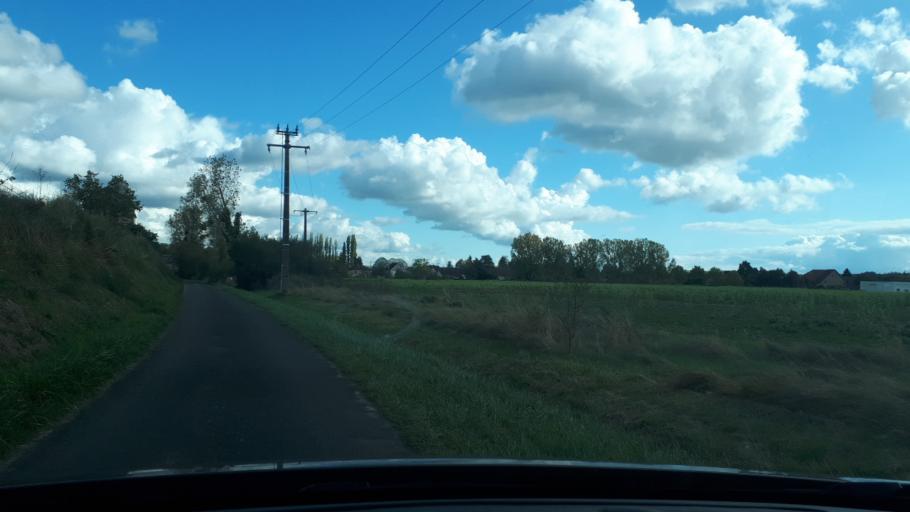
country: FR
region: Centre
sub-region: Departement du Loir-et-Cher
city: Saint-Aignan
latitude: 47.2878
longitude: 1.3801
